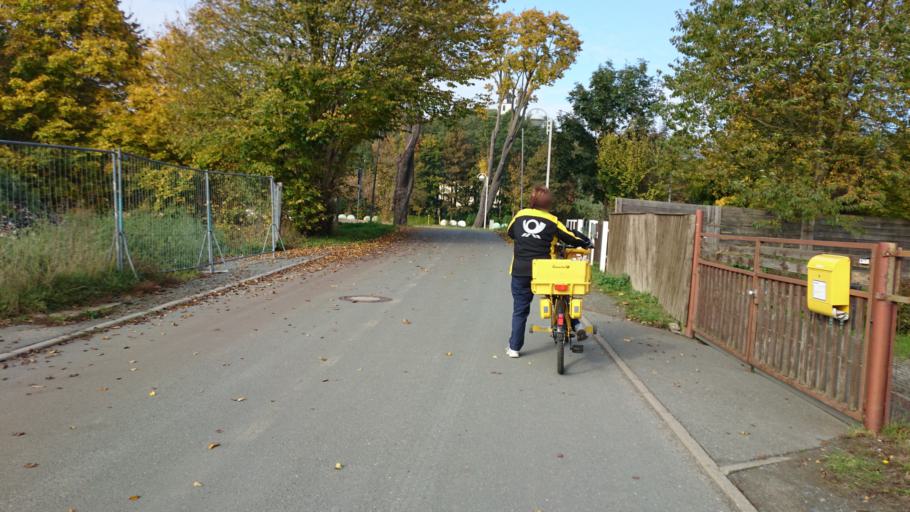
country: DE
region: Thuringia
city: Schleiz
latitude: 50.5808
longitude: 11.8059
